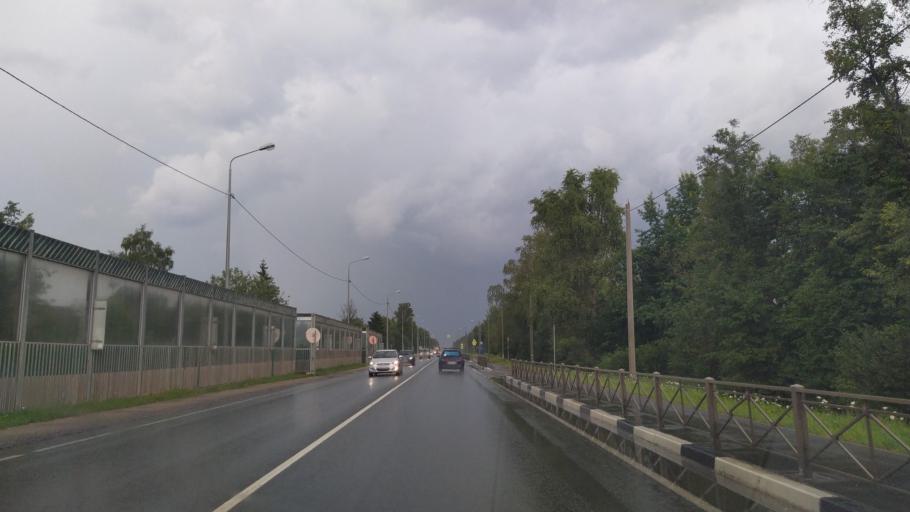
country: RU
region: Pskov
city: Pskov
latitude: 57.7609
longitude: 28.3860
